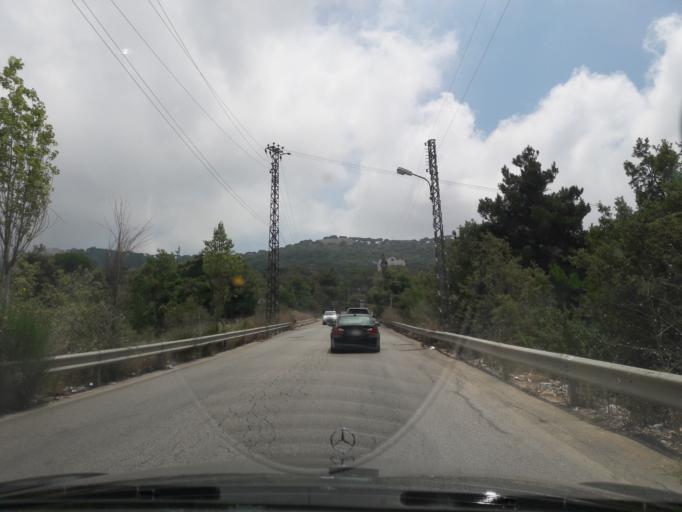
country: LB
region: Mont-Liban
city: Djounie
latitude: 33.9161
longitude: 35.6860
